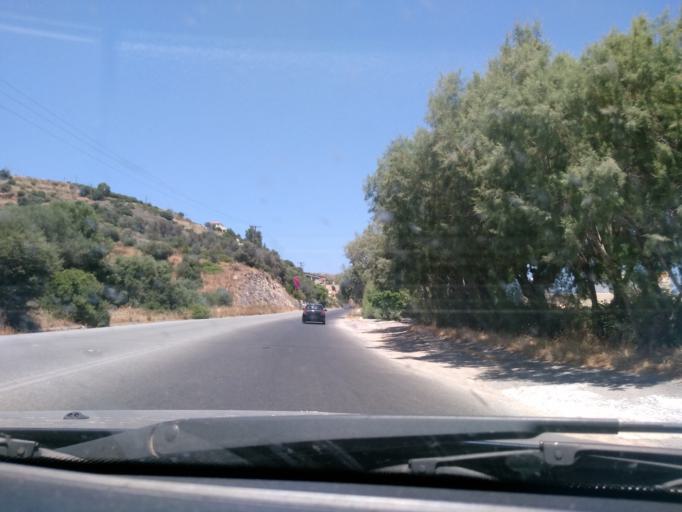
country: GR
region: Crete
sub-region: Nomos Irakleiou
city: Gazi
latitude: 35.3600
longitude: 25.0386
